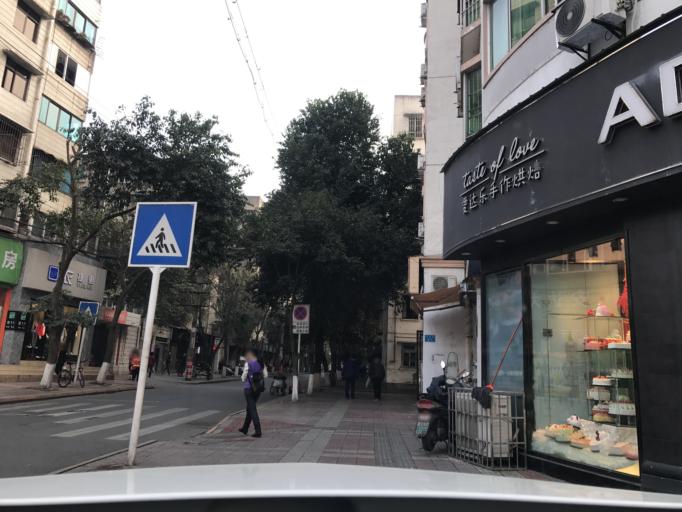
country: CN
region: Sichuan
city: Mianyang
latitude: 31.4538
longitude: 104.7551
